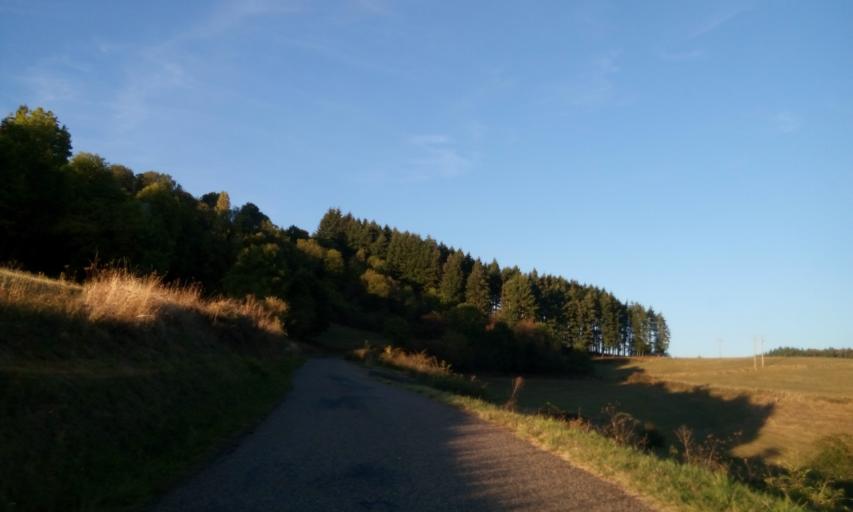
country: FR
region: Rhone-Alpes
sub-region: Departement du Rhone
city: Grandris
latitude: 45.9675
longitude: 4.4680
